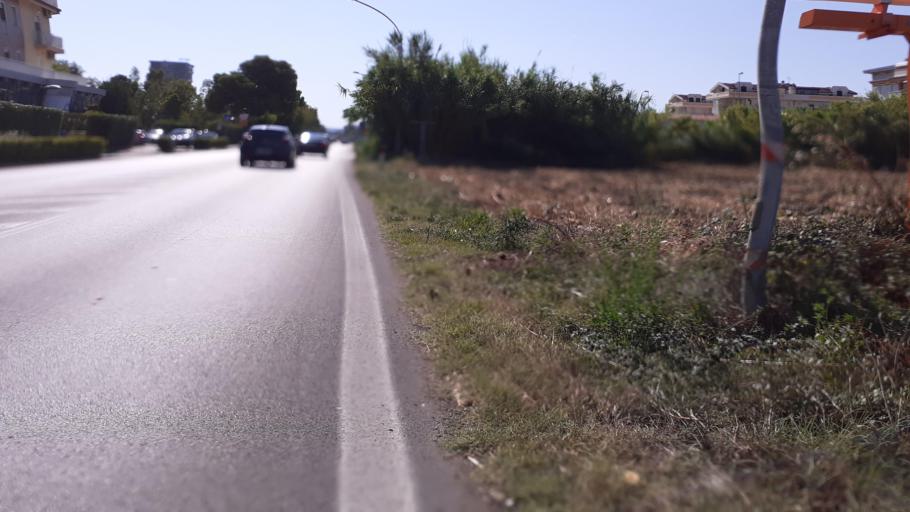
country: IT
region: Abruzzo
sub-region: Provincia di Chieti
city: Marina di Vasto
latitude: 42.0816
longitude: 14.7434
